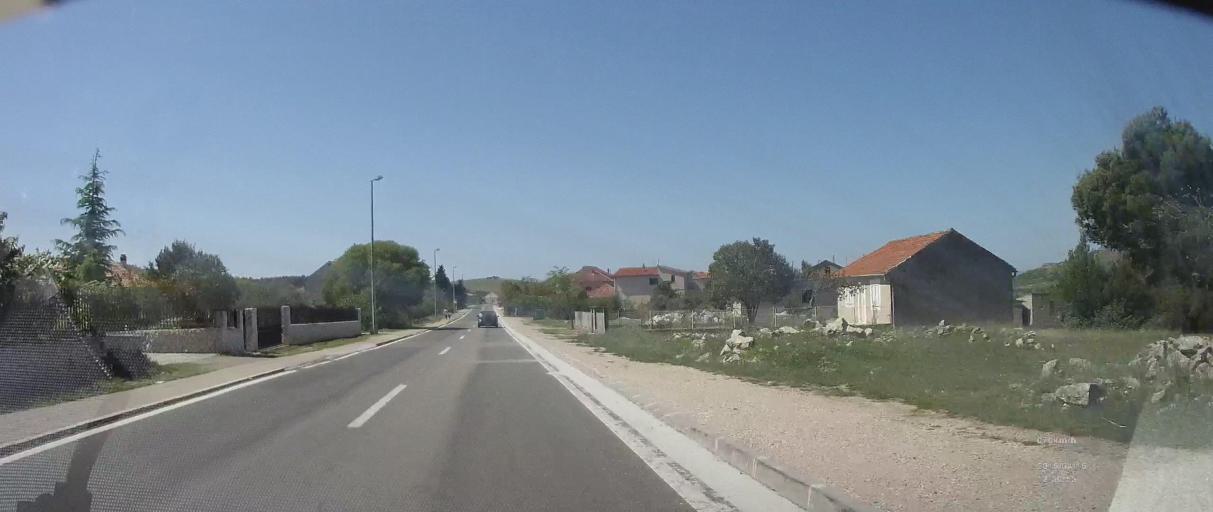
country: HR
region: Sibensko-Kniniska
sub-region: Grad Sibenik
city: Brodarica
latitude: 43.6748
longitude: 16.0093
